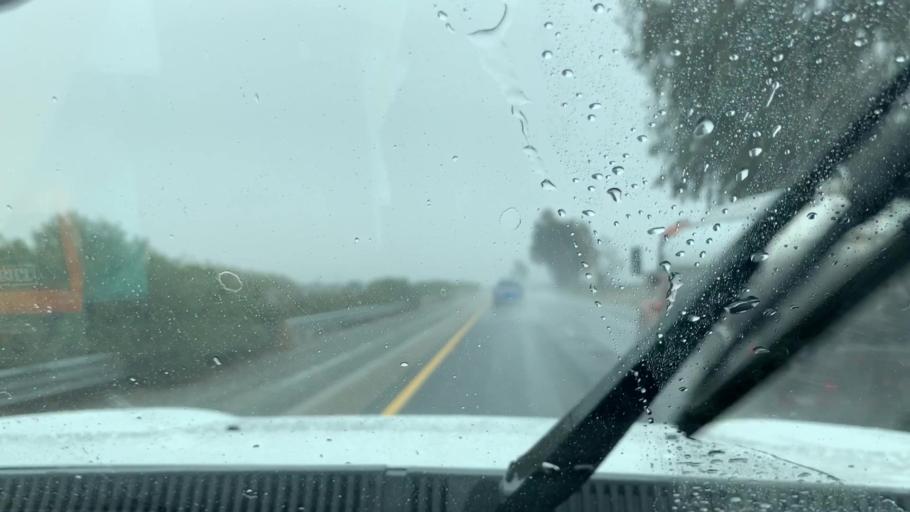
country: US
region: California
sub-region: Tulare County
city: Earlimart
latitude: 35.8462
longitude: -119.2653
